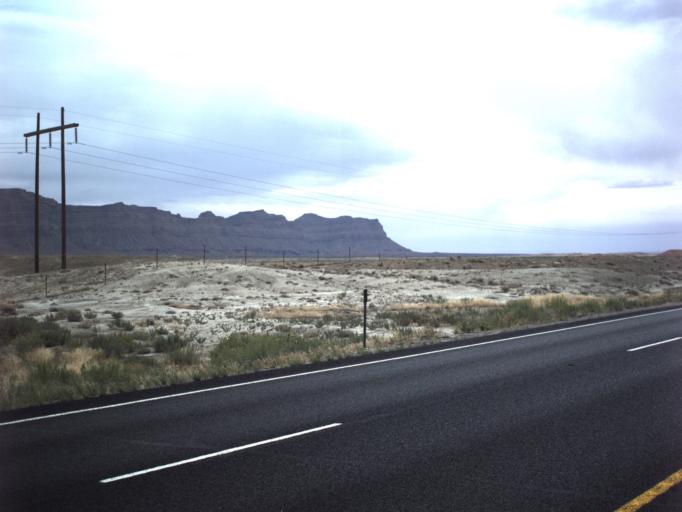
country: US
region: Utah
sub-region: Carbon County
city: East Carbon City
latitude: 39.1692
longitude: -110.3383
